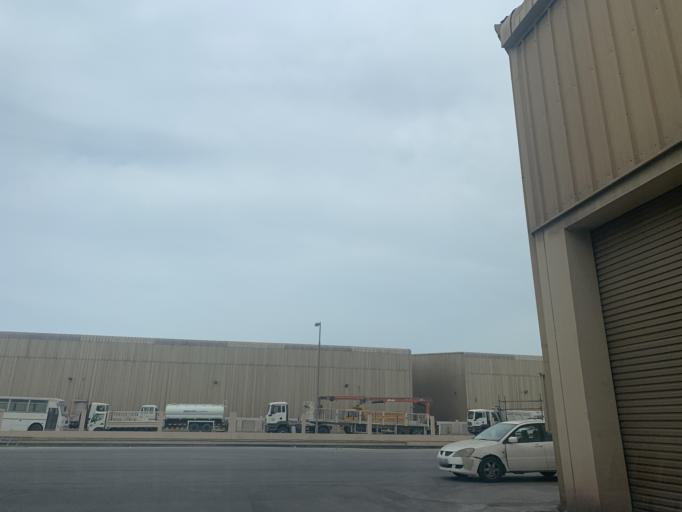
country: BH
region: Muharraq
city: Al Hadd
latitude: 26.2045
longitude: 50.6831
